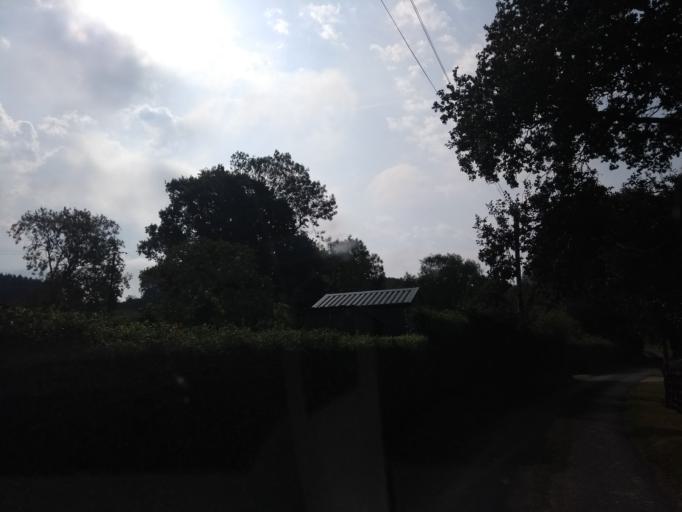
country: GB
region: England
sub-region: Somerset
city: Chard
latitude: 50.8827
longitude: -3.0429
